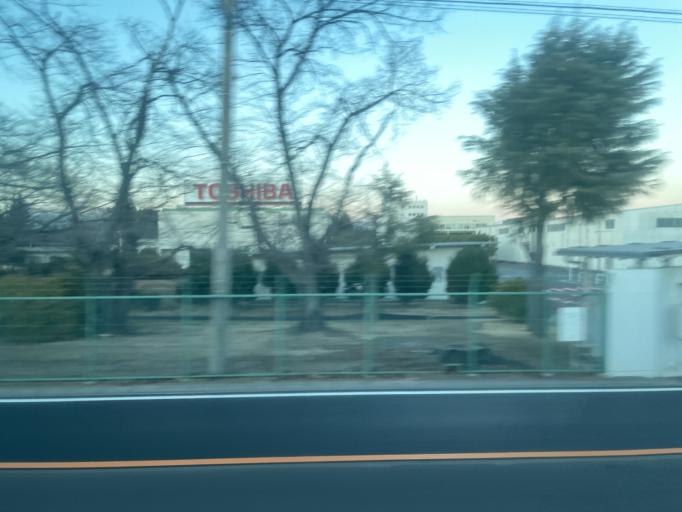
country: JP
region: Saitama
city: Fukayacho
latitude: 36.1819
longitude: 139.3130
